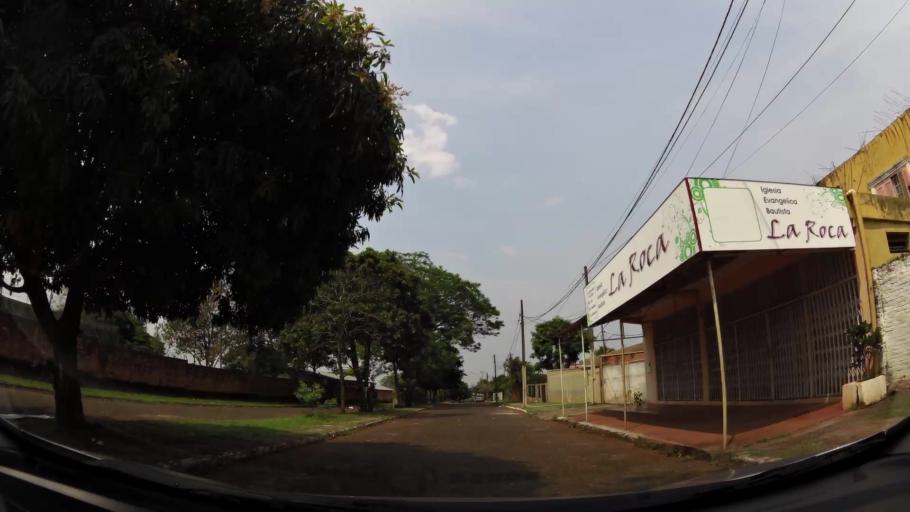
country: PY
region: Alto Parana
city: Presidente Franco
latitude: -25.5387
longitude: -54.6297
